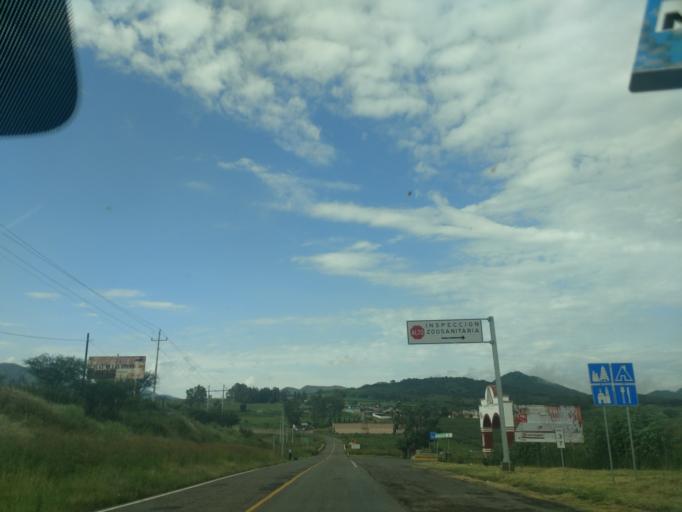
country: MX
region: Jalisco
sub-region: Atengo
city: Soyatlan del Oro
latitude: 20.5263
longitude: -104.3357
